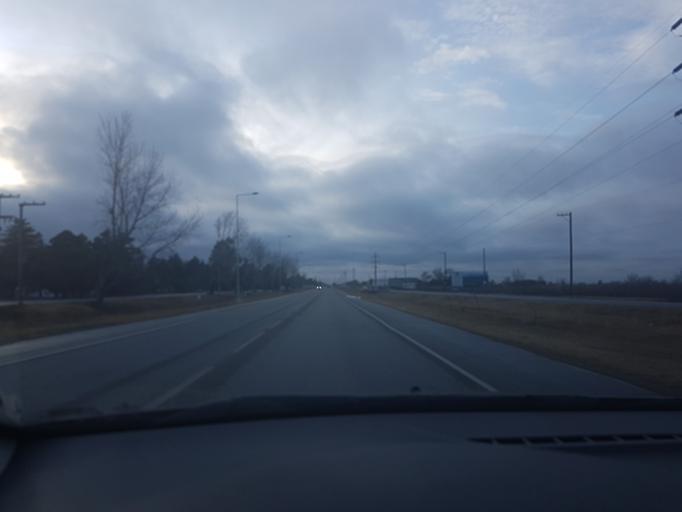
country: AR
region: Cordoba
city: Villa Allende
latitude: -31.3011
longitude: -64.2699
